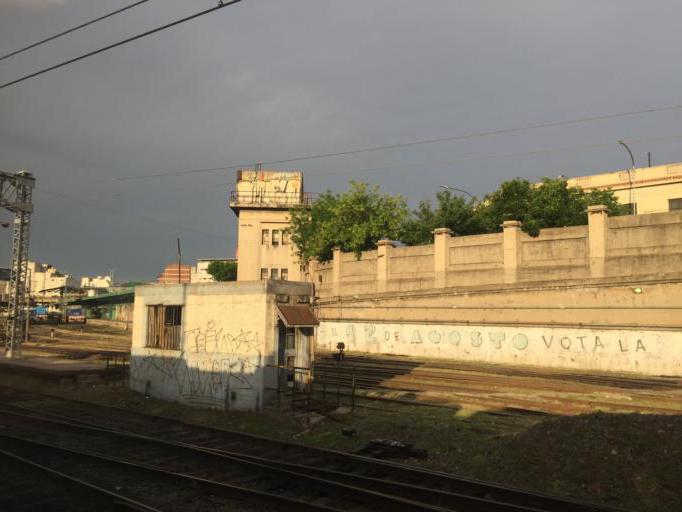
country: AR
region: Buenos Aires F.D.
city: Buenos Aires
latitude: -34.6329
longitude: -58.3805
